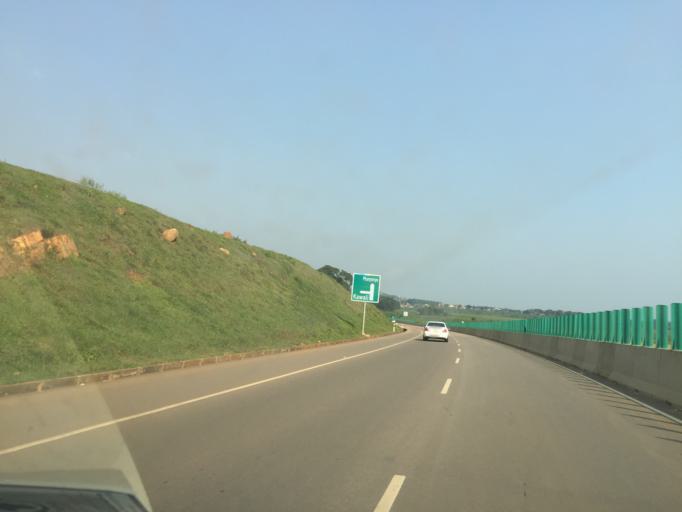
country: UG
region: Central Region
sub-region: Wakiso District
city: Kajansi
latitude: 0.2079
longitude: 32.5481
